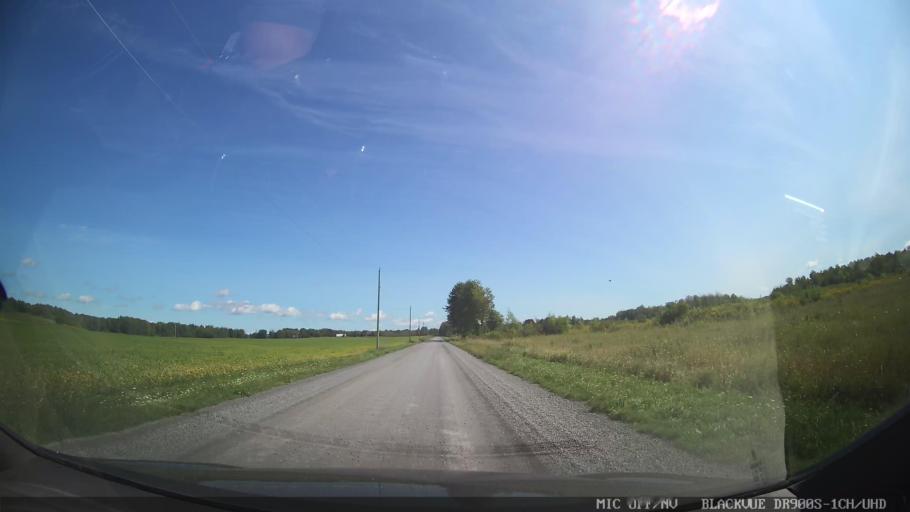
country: CA
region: Ontario
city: Bells Corners
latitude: 45.0854
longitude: -75.6740
